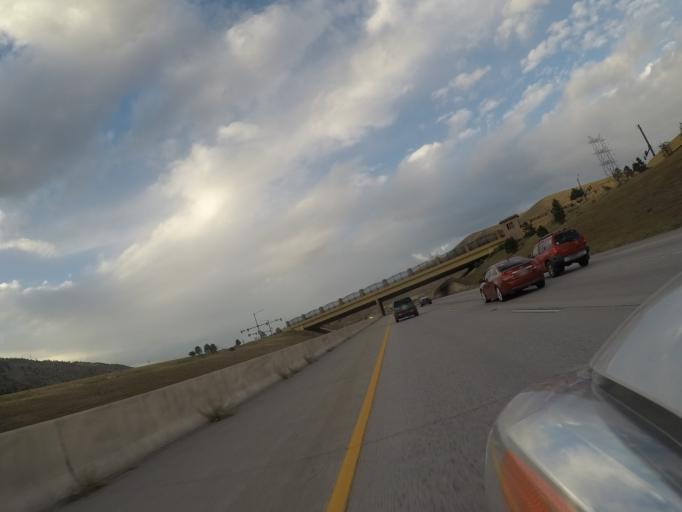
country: US
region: Colorado
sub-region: Jefferson County
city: West Pleasant View
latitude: 39.6857
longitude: -105.1880
